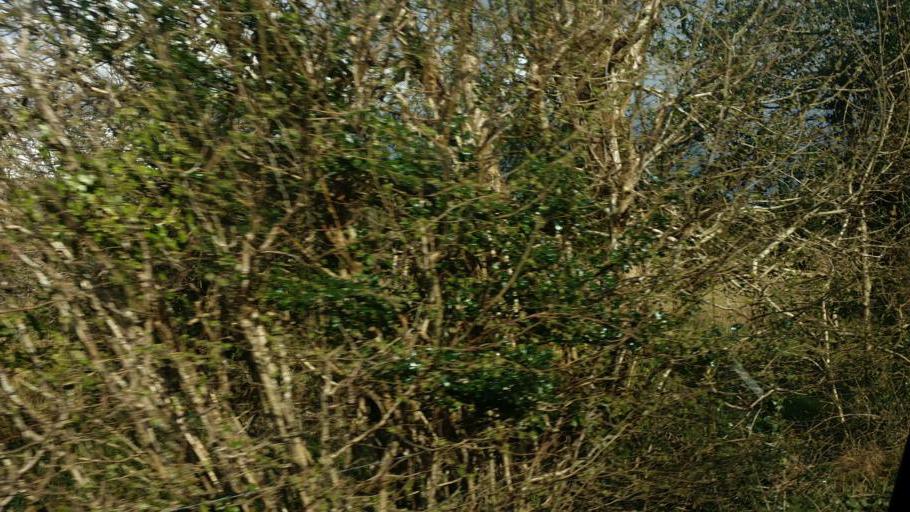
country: IE
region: Connaught
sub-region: County Leitrim
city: Manorhamilton
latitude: 54.3327
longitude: -8.2160
